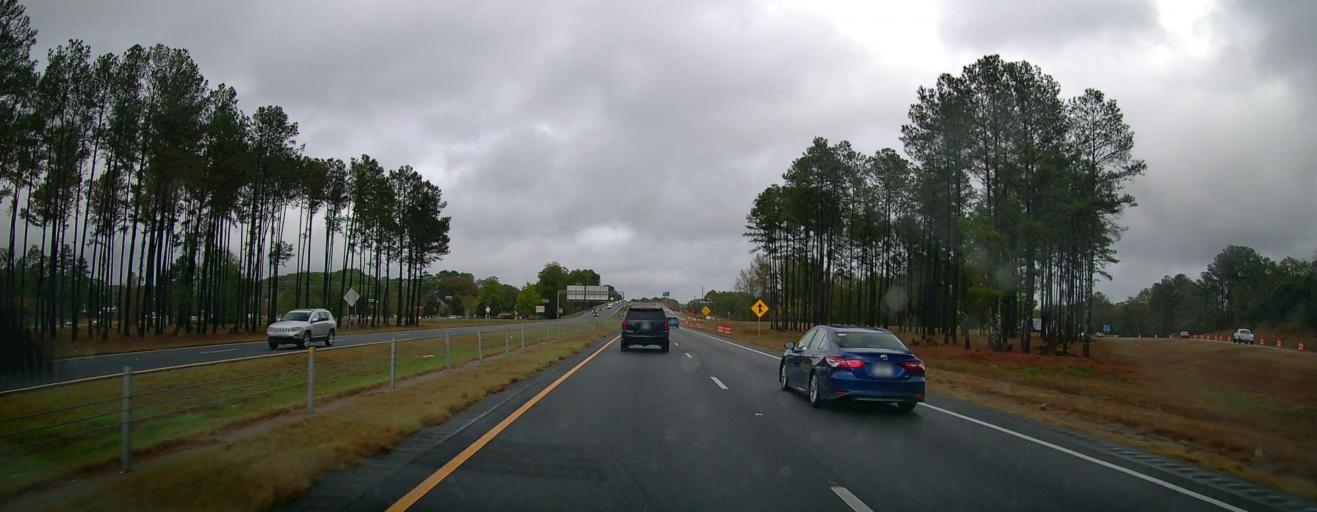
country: US
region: Georgia
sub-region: Clarke County
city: Athens
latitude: 33.9443
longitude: -83.3595
